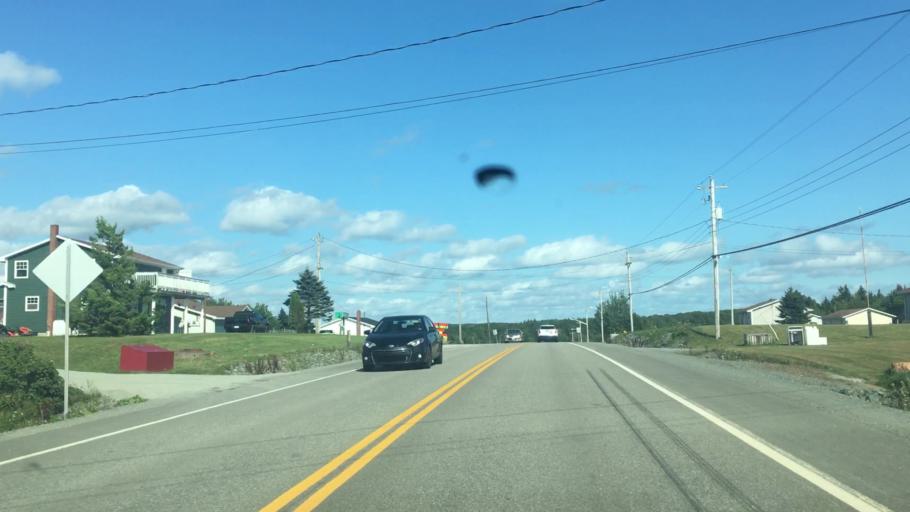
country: CA
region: Nova Scotia
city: Princeville
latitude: 45.6839
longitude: -60.7638
